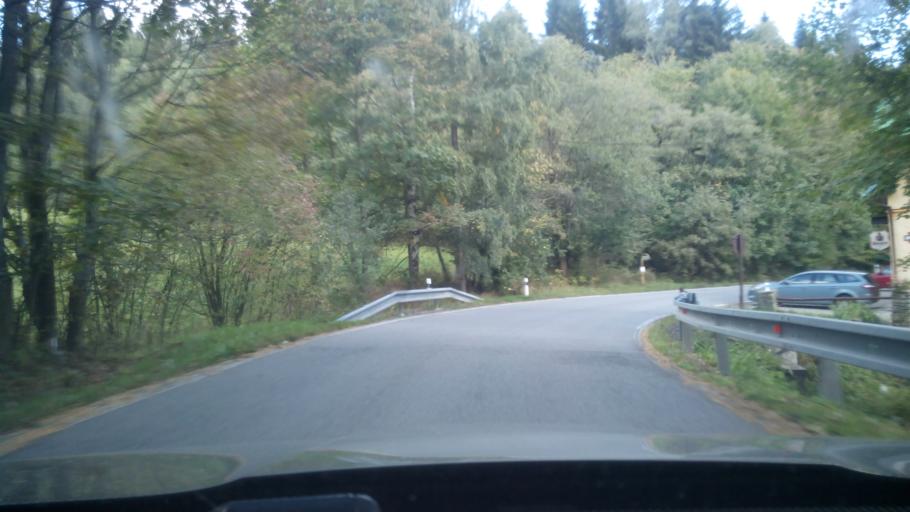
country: CZ
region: Plzensky
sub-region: Okres Klatovy
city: Kasperske Hory
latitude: 49.1436
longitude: 13.5963
